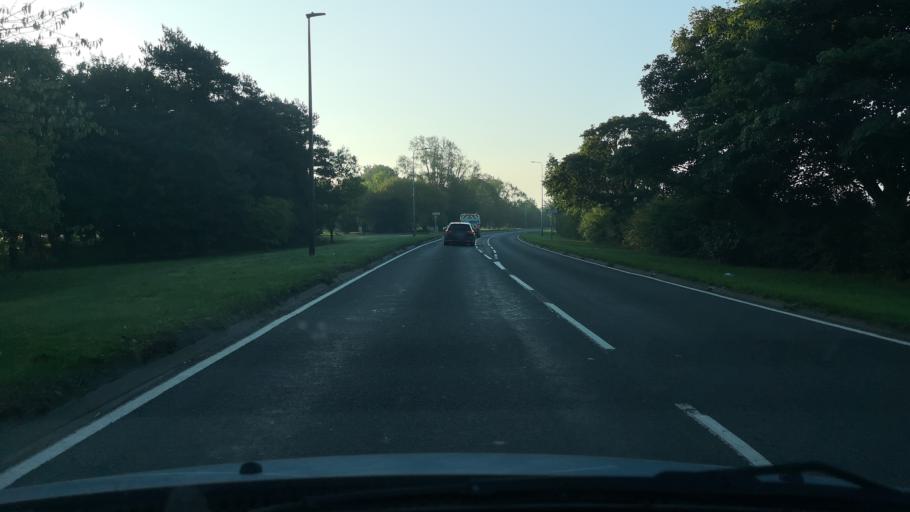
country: GB
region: England
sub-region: North Lincolnshire
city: Crowle
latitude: 53.5972
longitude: -0.8226
